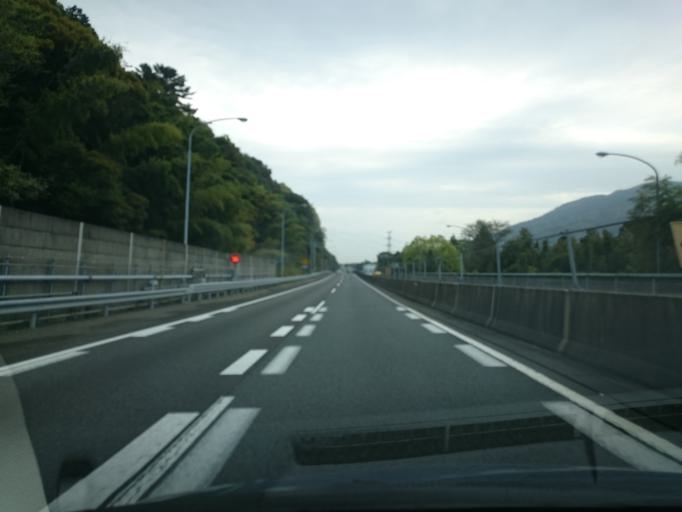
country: JP
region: Gifu
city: Tarui
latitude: 35.3437
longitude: 136.4922
